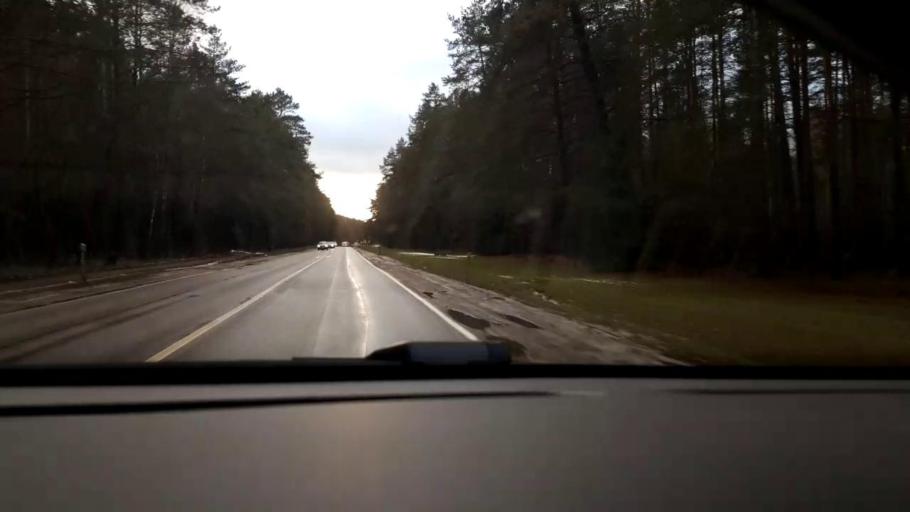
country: LT
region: Vilnius County
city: Rasos
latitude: 54.7664
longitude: 25.3774
